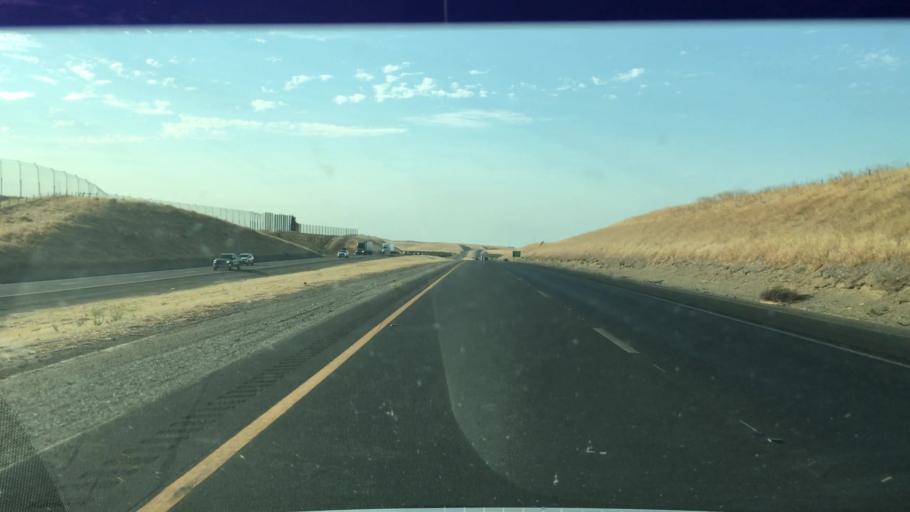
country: US
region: California
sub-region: Stanislaus County
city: Patterson
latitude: 37.3905
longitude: -121.1332
